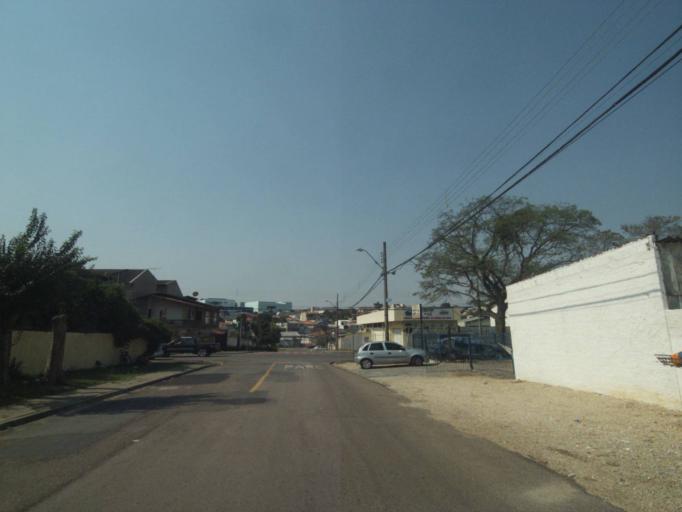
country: BR
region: Parana
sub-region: Sao Jose Dos Pinhais
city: Sao Jose dos Pinhais
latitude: -25.5109
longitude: -49.2766
